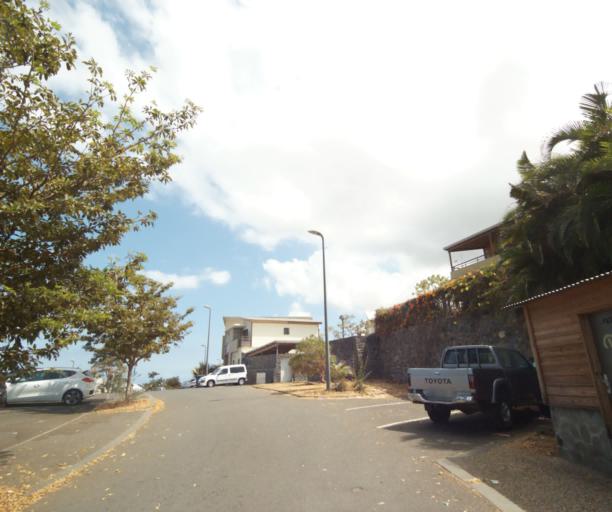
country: RE
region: Reunion
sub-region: Reunion
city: Trois-Bassins
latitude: -21.0870
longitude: 55.2391
